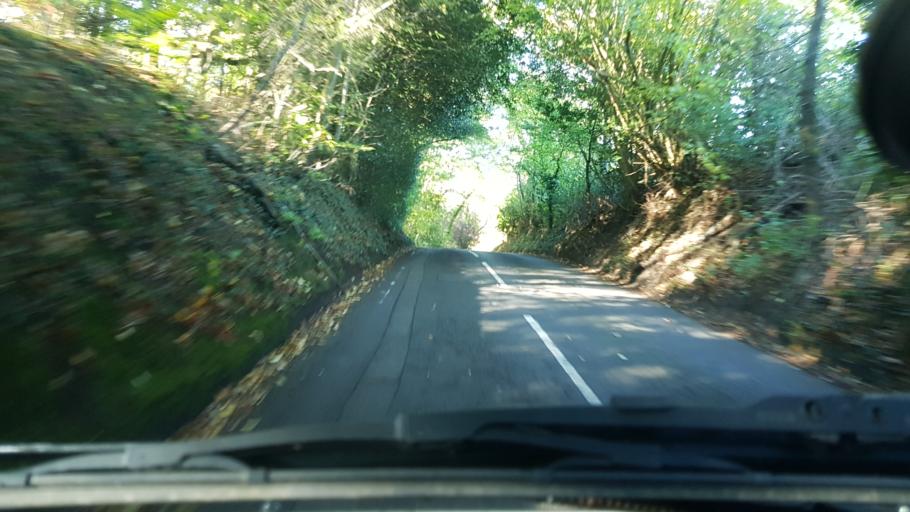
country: GB
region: England
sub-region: Surrey
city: Pirbright
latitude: 51.2683
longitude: -0.6461
